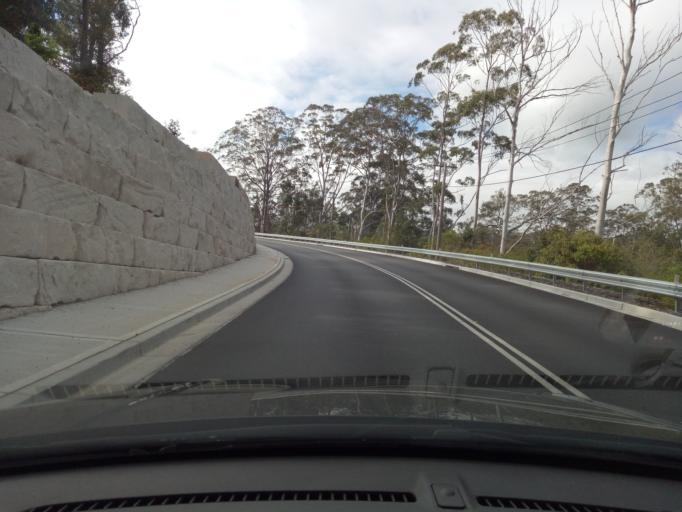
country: AU
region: New South Wales
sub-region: Gosford Shire
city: Lisarow
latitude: -33.3898
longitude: 151.3820
